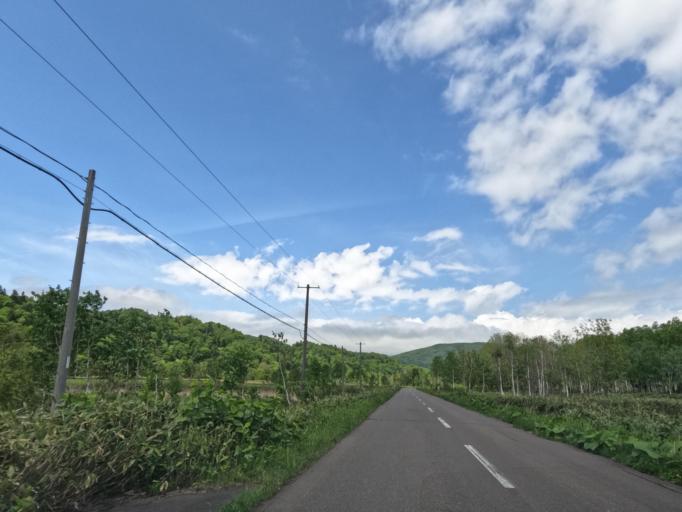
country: JP
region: Hokkaido
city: Tobetsu
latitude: 43.5217
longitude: 141.5873
